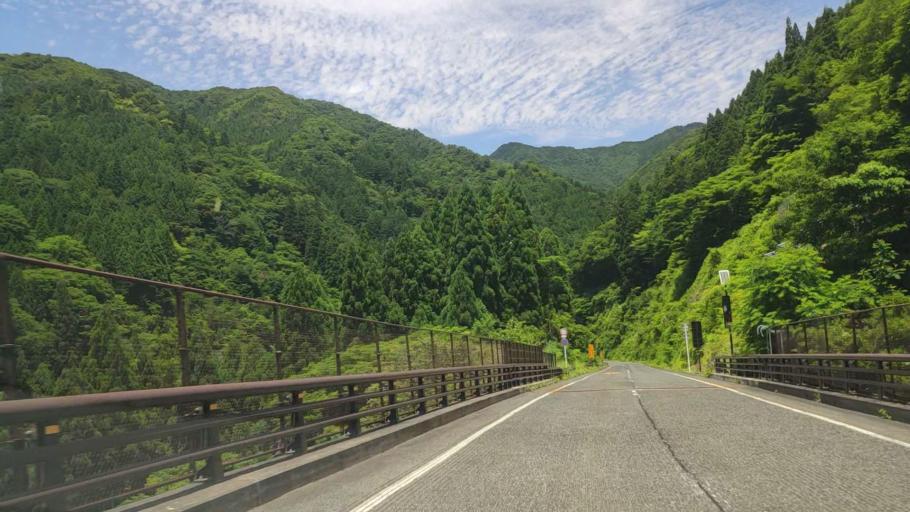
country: JP
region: Tottori
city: Tottori
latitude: 35.3468
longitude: 134.4507
